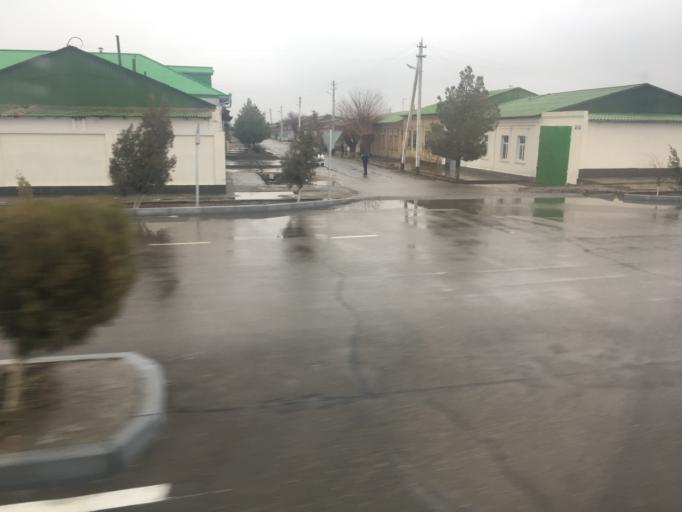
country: TM
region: Lebap
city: Turkmenabat
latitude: 39.0267
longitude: 63.5966
